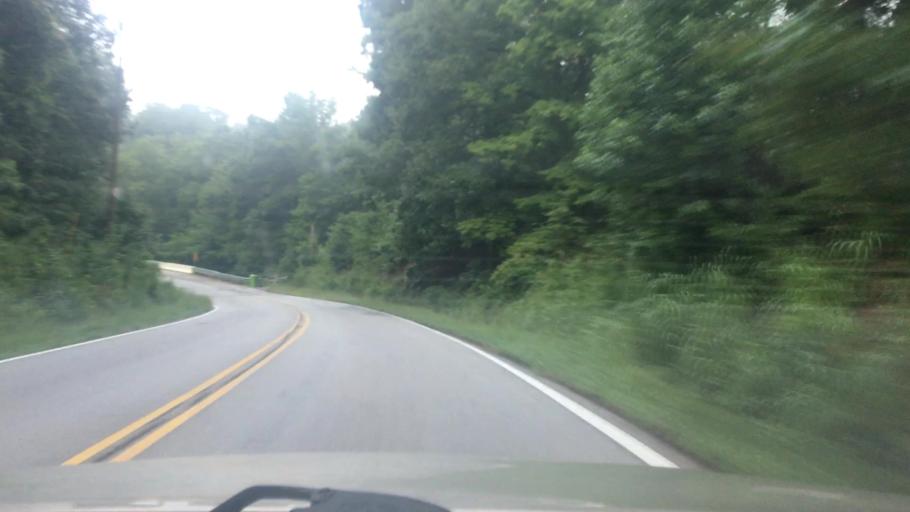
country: US
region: South Carolina
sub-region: Lexington County
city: Irmo
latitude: 34.1387
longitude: -81.1822
